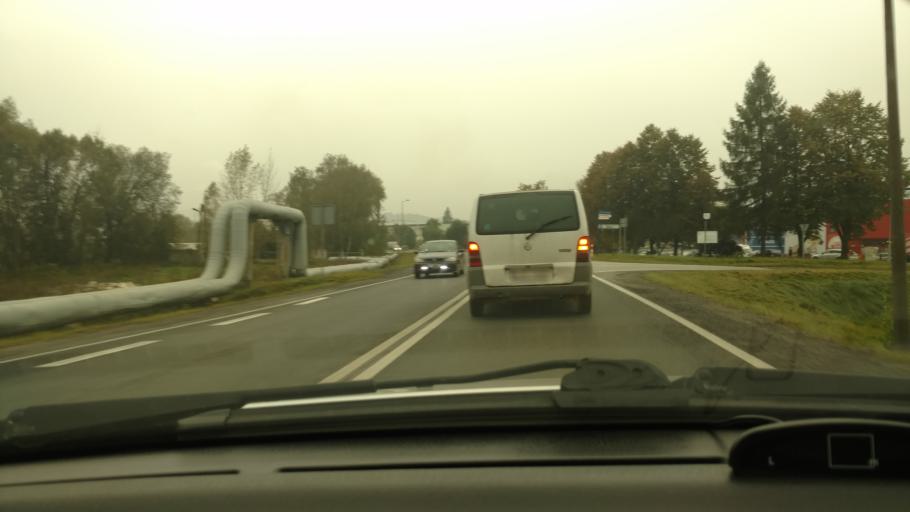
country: PL
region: Lesser Poland Voivodeship
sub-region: Powiat gorlicki
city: Gorlice
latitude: 49.6697
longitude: 21.1778
